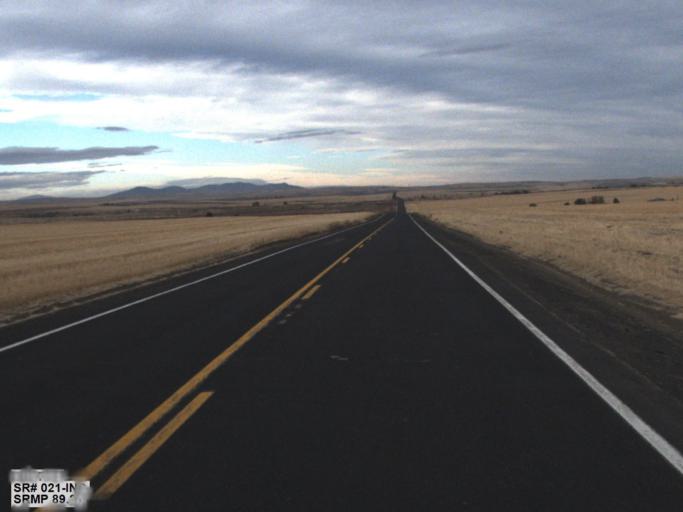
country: US
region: Washington
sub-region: Okanogan County
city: Coulee Dam
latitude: 47.7299
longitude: -118.7219
